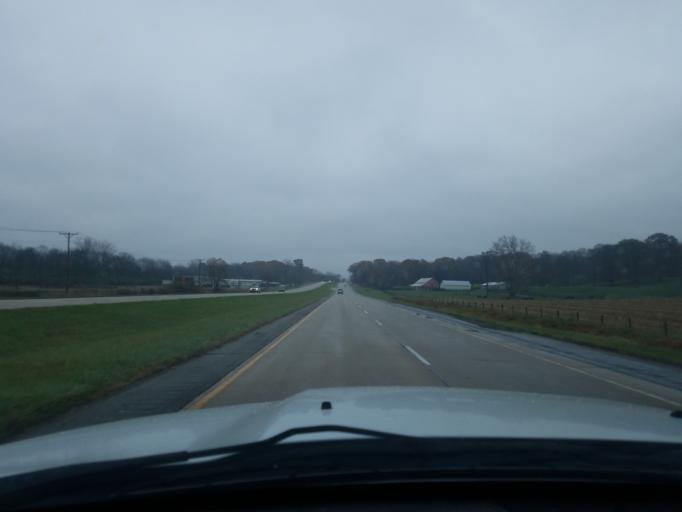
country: US
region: Indiana
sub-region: Cass County
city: Logansport
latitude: 40.7323
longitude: -86.3241
